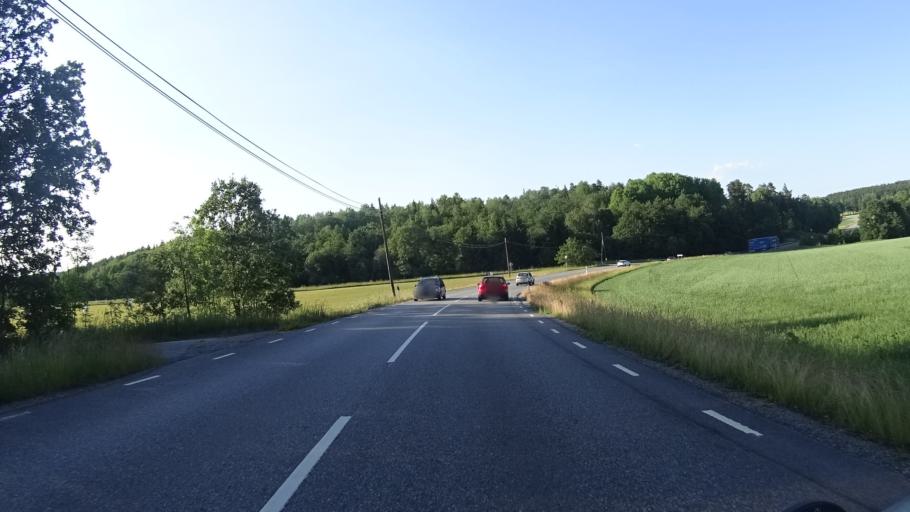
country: SE
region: Stockholm
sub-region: Sodertalje Kommun
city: Pershagen
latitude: 59.1063
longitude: 17.6353
